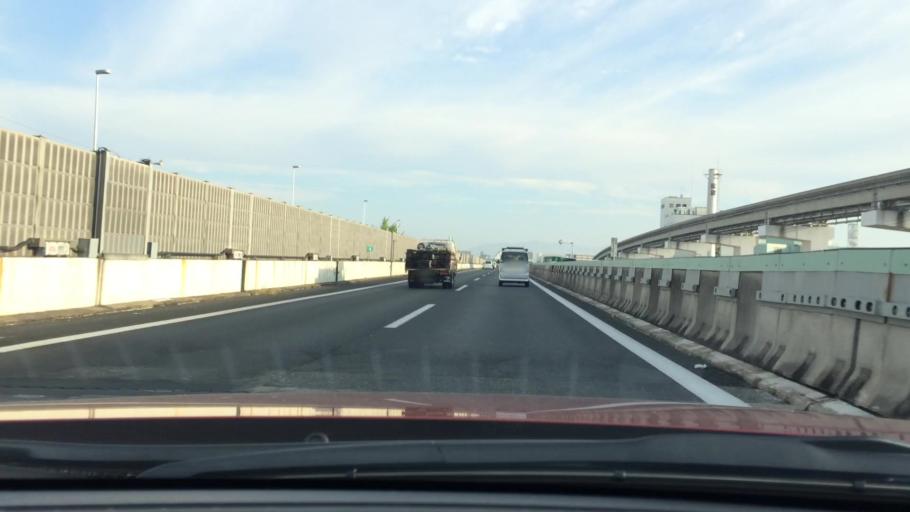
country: JP
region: Osaka
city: Ibaraki
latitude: 34.7876
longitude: 135.5635
